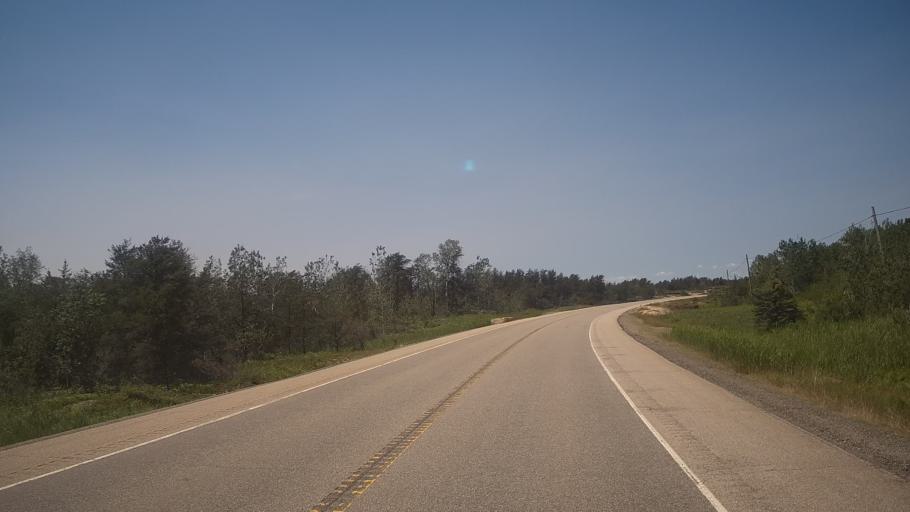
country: CA
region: Ontario
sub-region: Parry Sound District
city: Parry Sound
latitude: 45.7821
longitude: -80.5173
